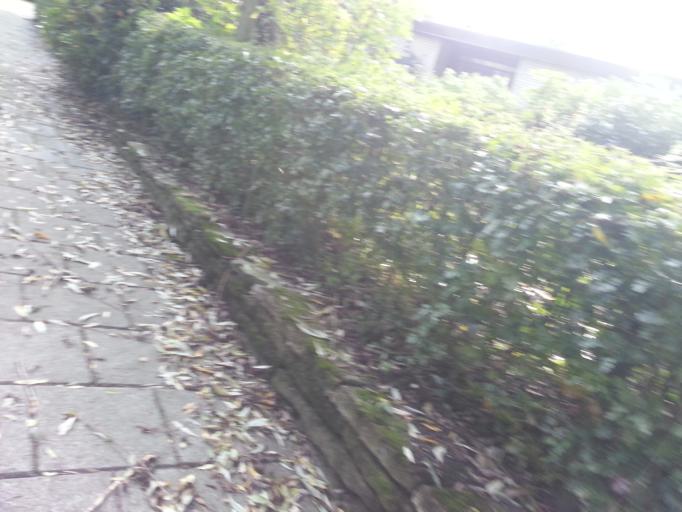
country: NL
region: North Brabant
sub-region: Gemeente Eindhoven
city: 't Hofke
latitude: 51.4728
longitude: 5.5008
